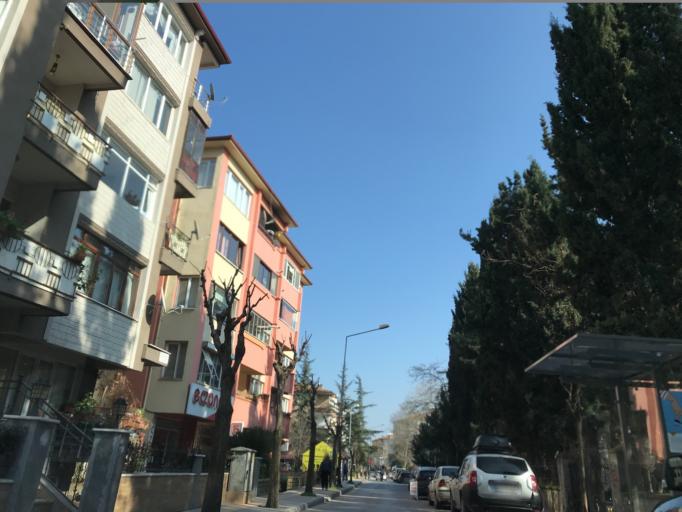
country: TR
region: Yalova
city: Yalova
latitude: 40.6543
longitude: 29.2624
